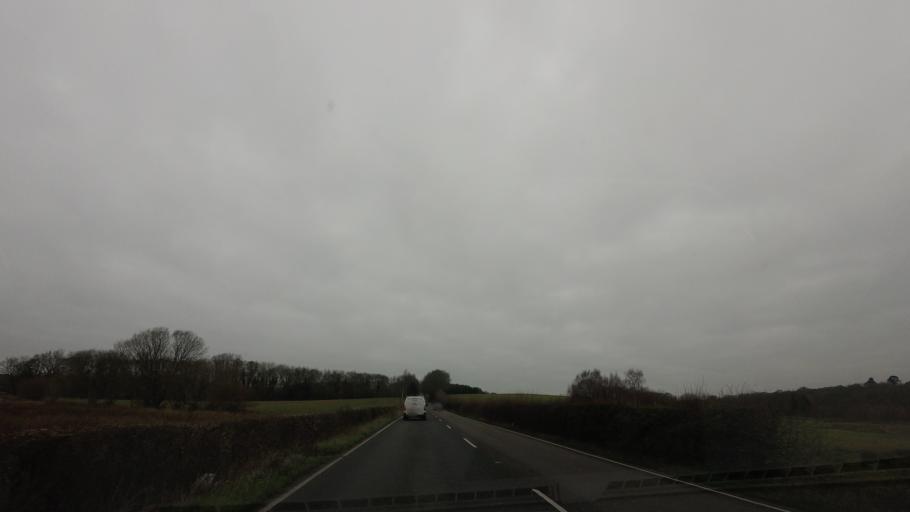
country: GB
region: England
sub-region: East Sussex
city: Battle
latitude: 50.9325
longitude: 0.5231
